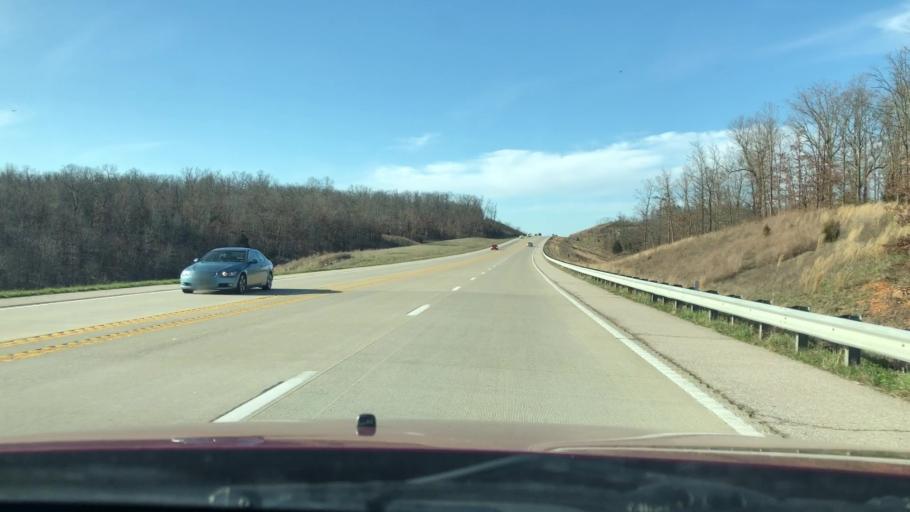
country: US
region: Missouri
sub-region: Camden County
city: Camdenton
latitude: 37.9296
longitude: -92.7135
